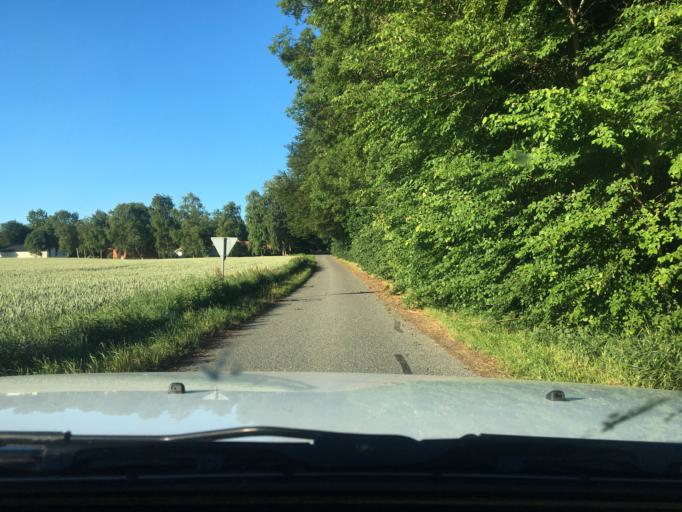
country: DK
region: Central Jutland
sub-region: Randers Kommune
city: Randers
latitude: 56.4101
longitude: 10.0540
